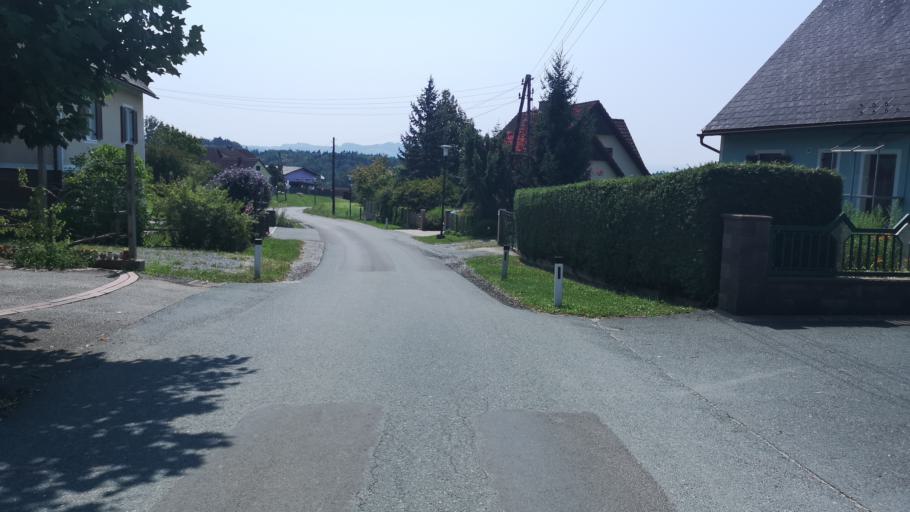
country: AT
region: Styria
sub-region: Politischer Bezirk Deutschlandsberg
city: Preding
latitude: 46.8646
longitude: 15.3893
